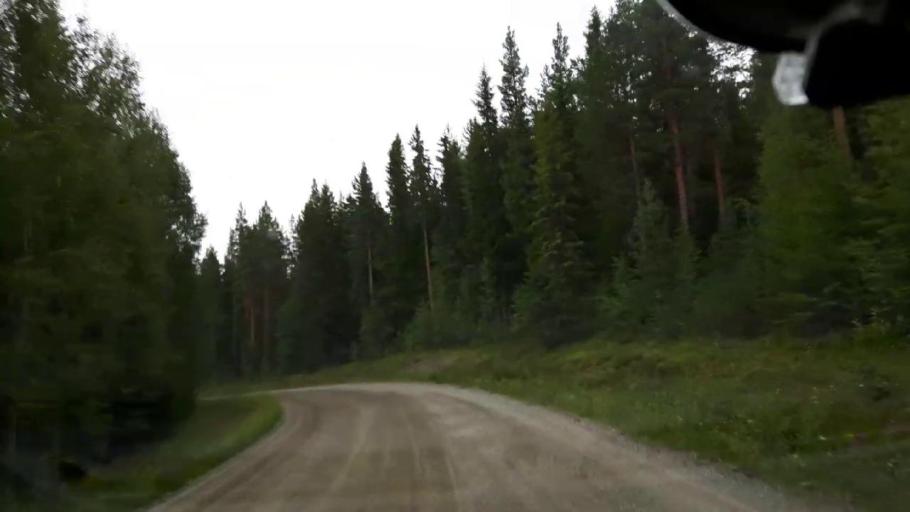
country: SE
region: Jaemtland
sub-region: Braecke Kommun
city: Braecke
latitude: 62.9134
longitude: 15.5792
